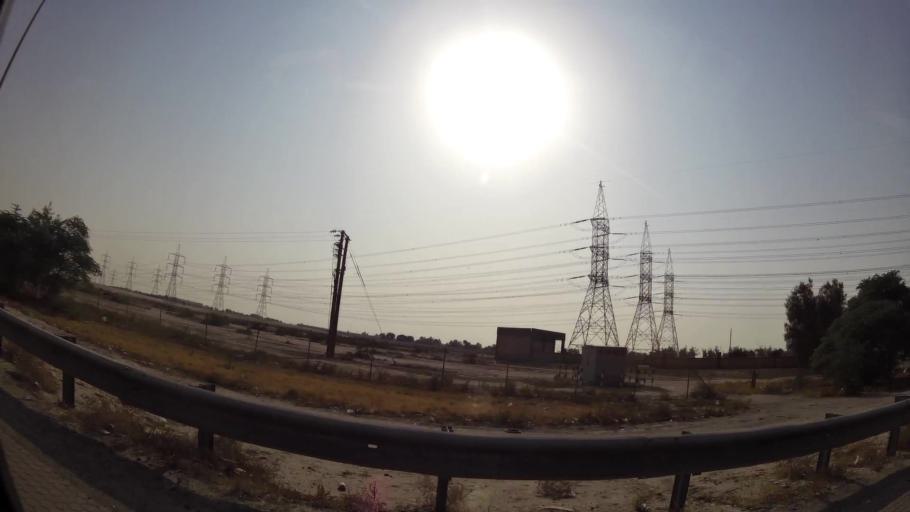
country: KW
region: Muhafazat al Jahra'
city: Al Jahra'
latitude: 29.3102
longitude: 47.7828
